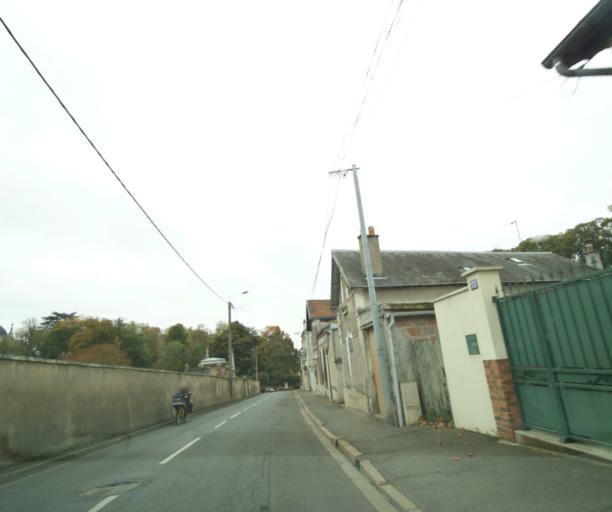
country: FR
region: Centre
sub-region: Departement d'Eure-et-Loir
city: Dreux
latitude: 48.7402
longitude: 1.3635
